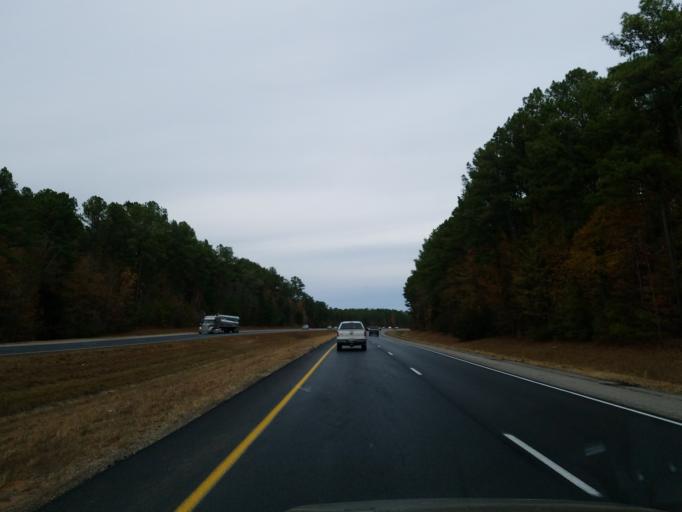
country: US
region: Mississippi
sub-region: Clarke County
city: Stonewall
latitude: 32.2325
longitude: -88.8319
